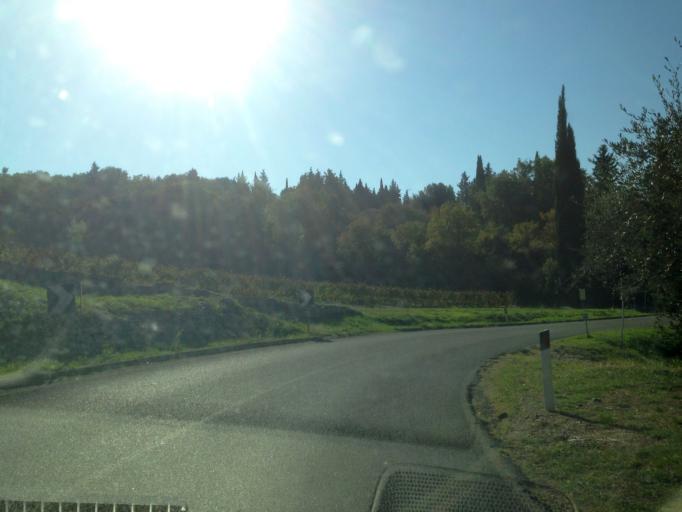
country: IT
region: Tuscany
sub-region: Provincia di Siena
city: Castellina in Chianti
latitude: 43.4383
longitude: 11.3081
